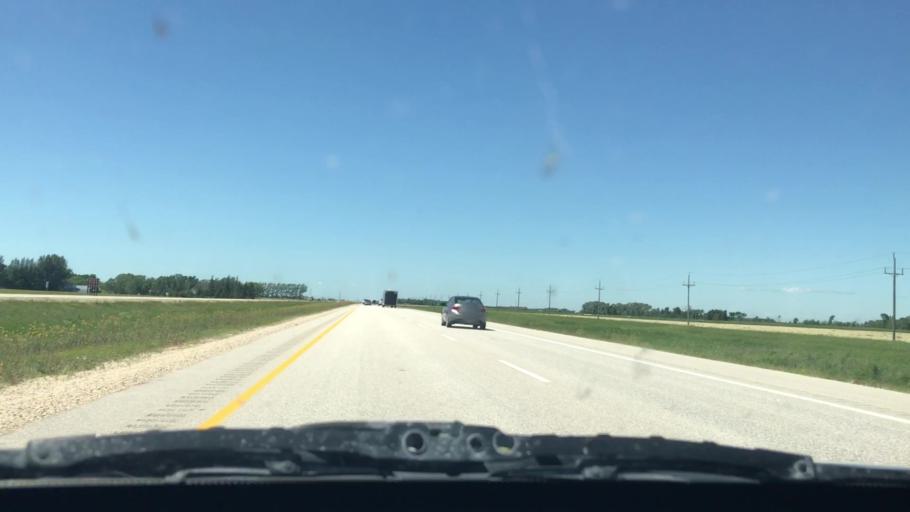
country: CA
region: Manitoba
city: Steinbach
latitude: 49.7296
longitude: -96.7171
